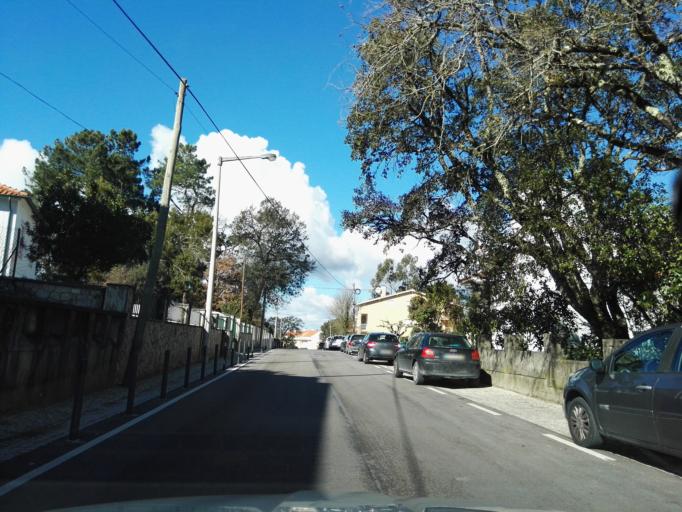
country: PT
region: Santarem
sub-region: Ourem
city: Fatima
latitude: 39.6337
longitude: -8.6778
